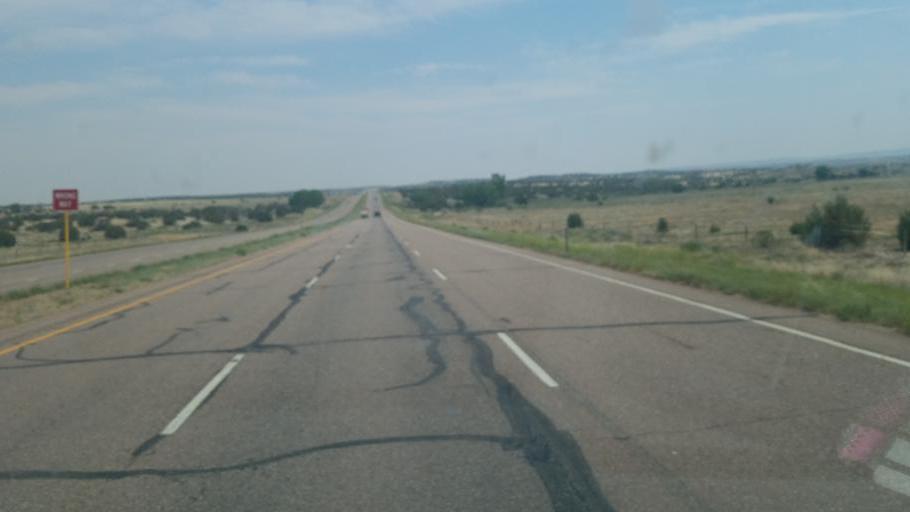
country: US
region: Colorado
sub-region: Fremont County
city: Penrose
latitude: 38.3911
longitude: -104.9680
